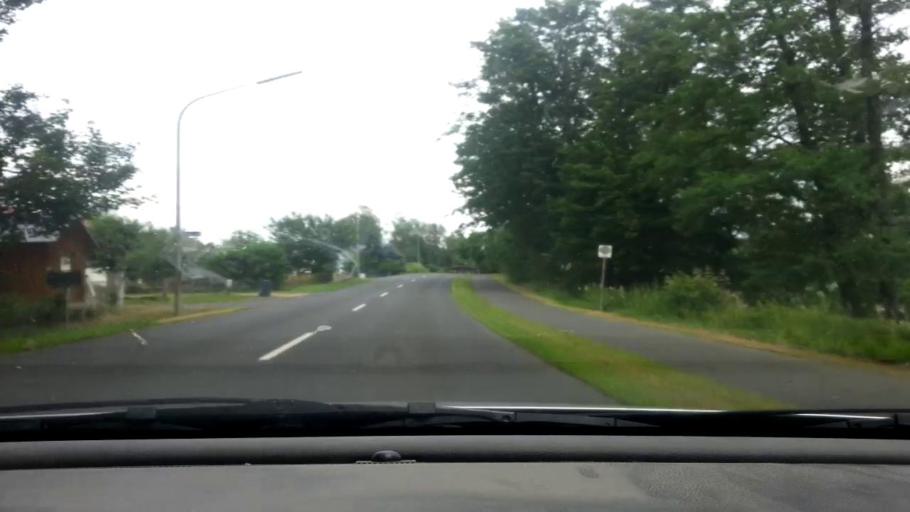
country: DE
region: Bavaria
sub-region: Upper Palatinate
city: Waldsassen
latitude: 50.0212
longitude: 12.3228
